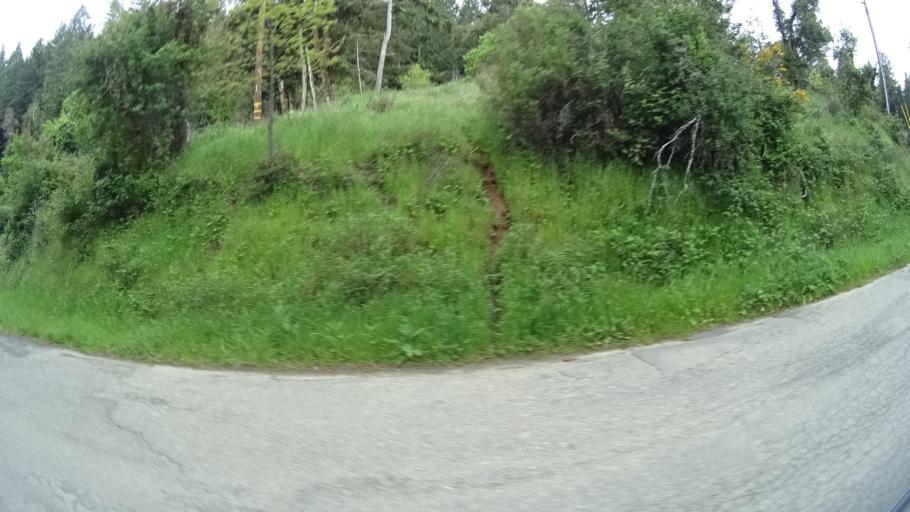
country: US
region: California
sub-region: Humboldt County
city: Redway
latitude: 40.3031
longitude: -123.8215
